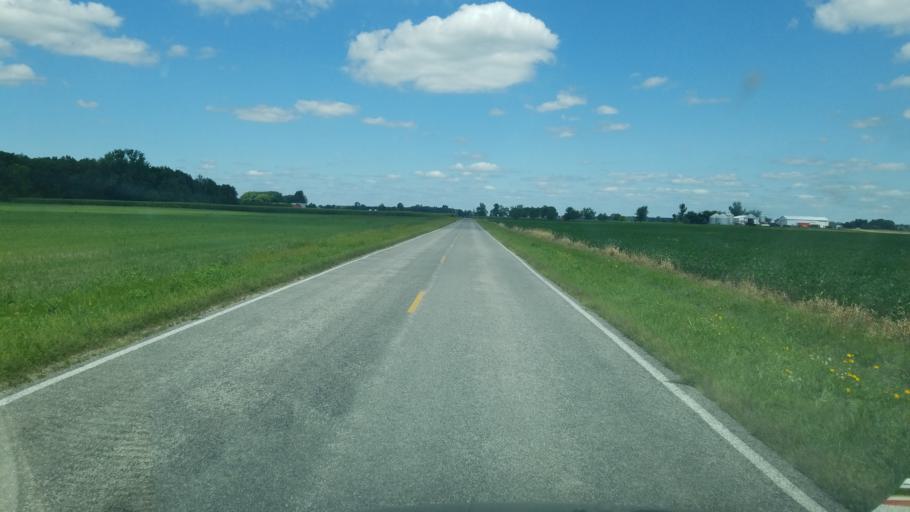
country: US
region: Ohio
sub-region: Fulton County
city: Delta
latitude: 41.6078
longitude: -84.0084
